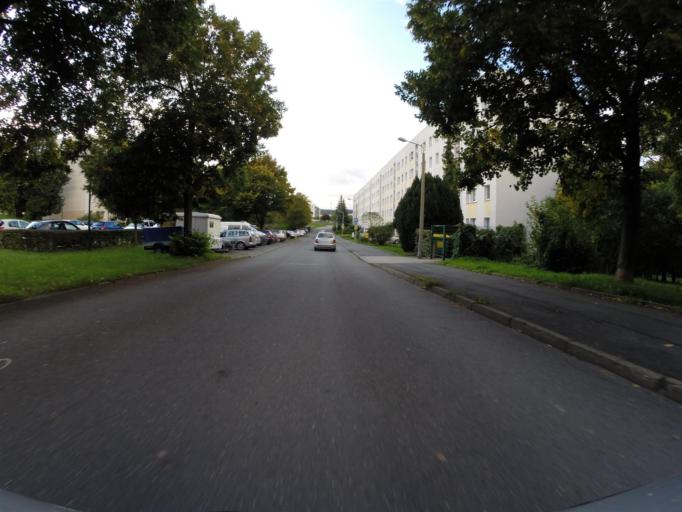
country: DE
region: Thuringia
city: Jena
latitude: 50.8930
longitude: 11.5802
